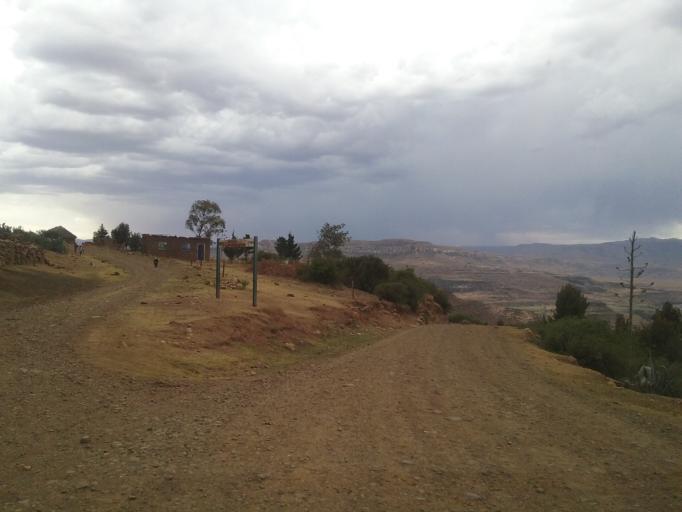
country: LS
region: Quthing
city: Quthing
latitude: -30.3075
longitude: 27.8100
